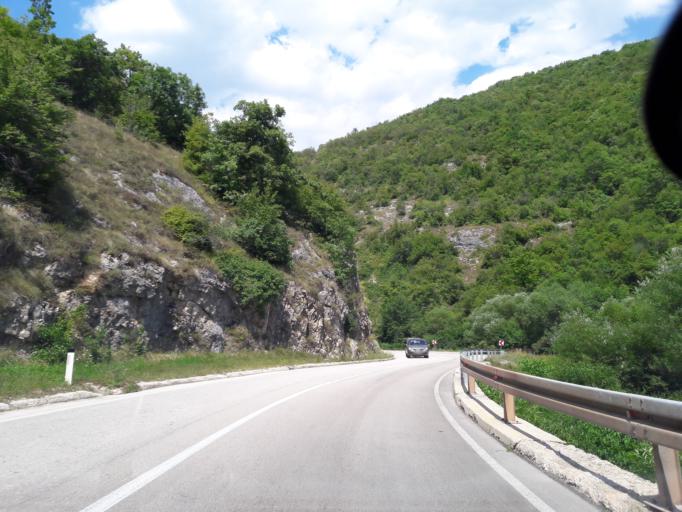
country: BA
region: Republika Srpska
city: Mrkonjic Grad
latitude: 44.4524
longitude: 17.1627
